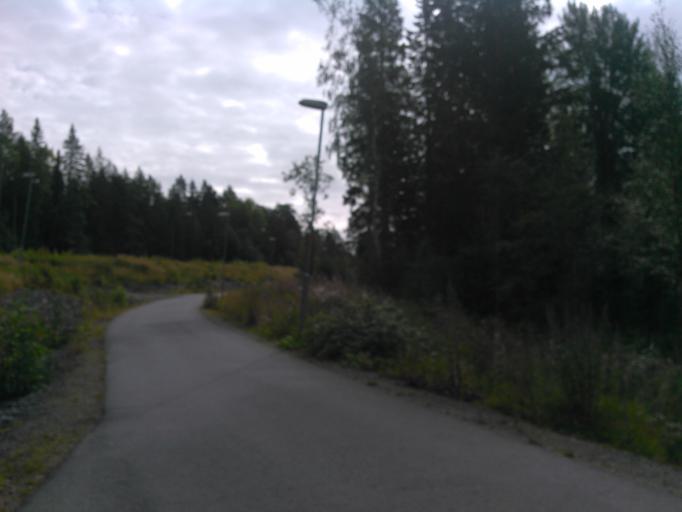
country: SE
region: Vaesterbotten
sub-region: Umea Kommun
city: Umea
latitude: 63.8250
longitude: 20.3116
